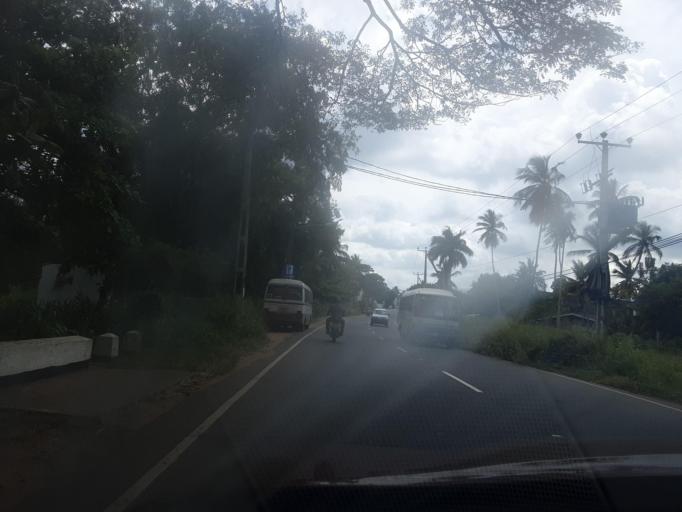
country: LK
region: North Western
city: Kuliyapitiya
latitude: 7.4734
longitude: 80.0208
